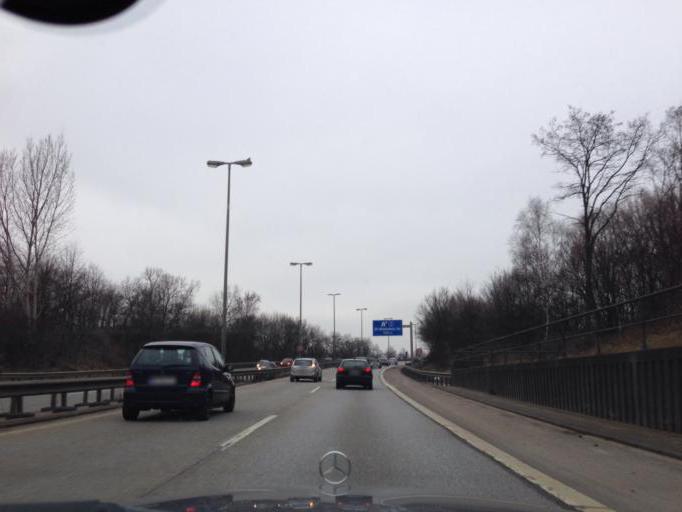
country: DE
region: Hamburg
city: Harburg
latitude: 53.4680
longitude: 9.9957
